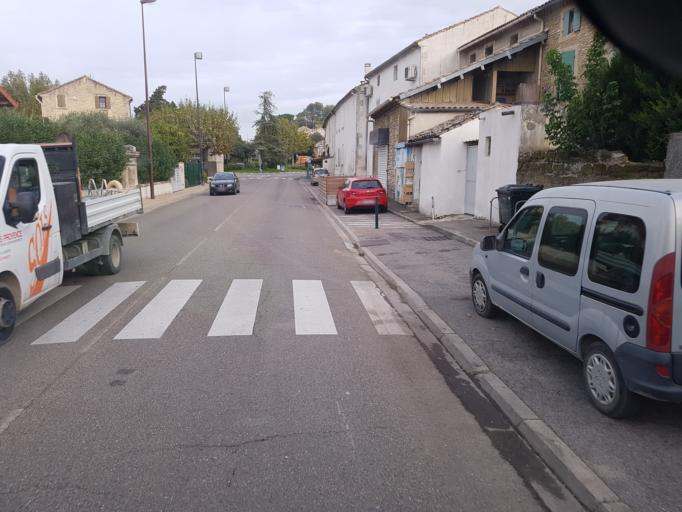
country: FR
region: Provence-Alpes-Cote d'Azur
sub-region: Departement des Bouches-du-Rhone
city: Barbentane
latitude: 43.9021
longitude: 4.7551
